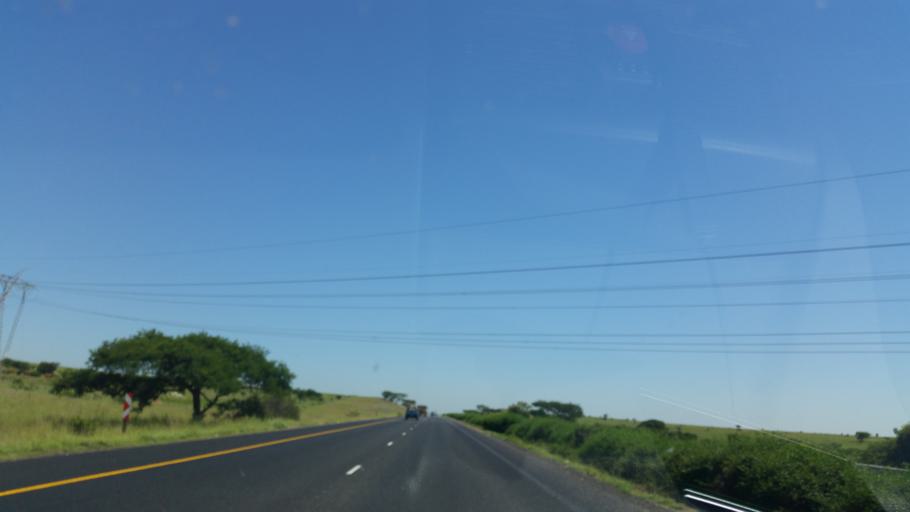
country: ZA
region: KwaZulu-Natal
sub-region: uThukela District Municipality
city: Ladysmith
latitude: -28.6461
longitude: 29.6221
